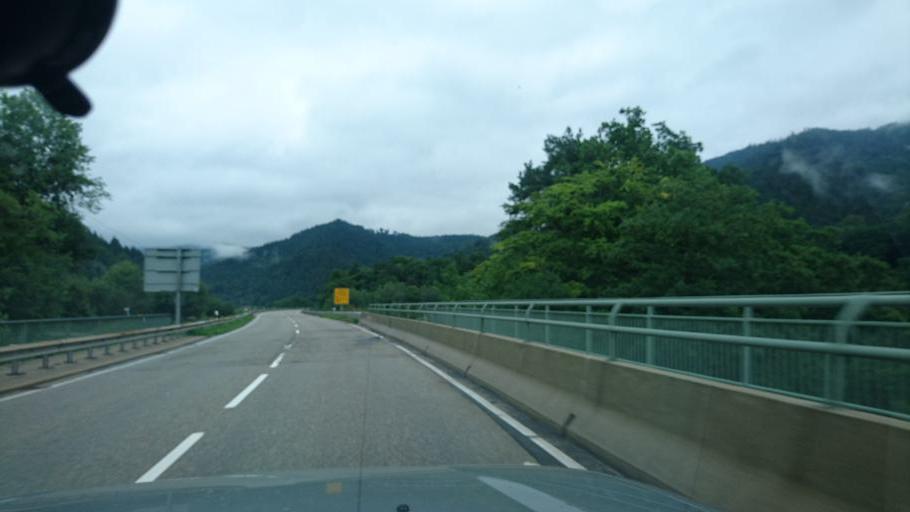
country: DE
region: Baden-Wuerttemberg
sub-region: Karlsruhe Region
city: Weisenbach
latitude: 48.7053
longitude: 8.3604
